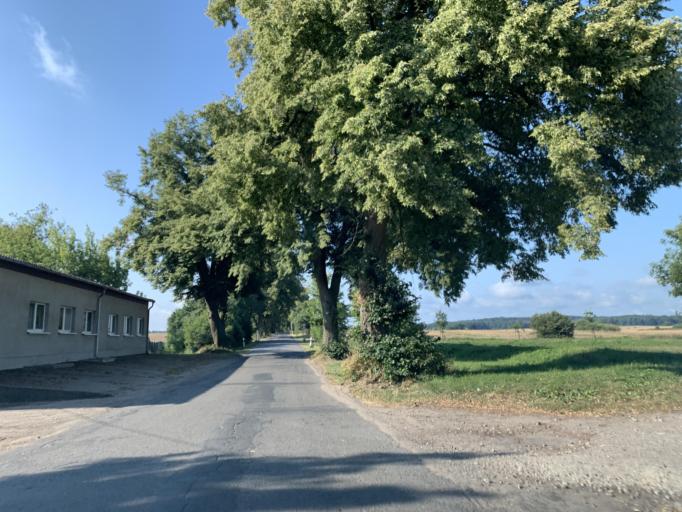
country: DE
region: Mecklenburg-Vorpommern
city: Blankensee
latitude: 53.3434
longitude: 13.3501
